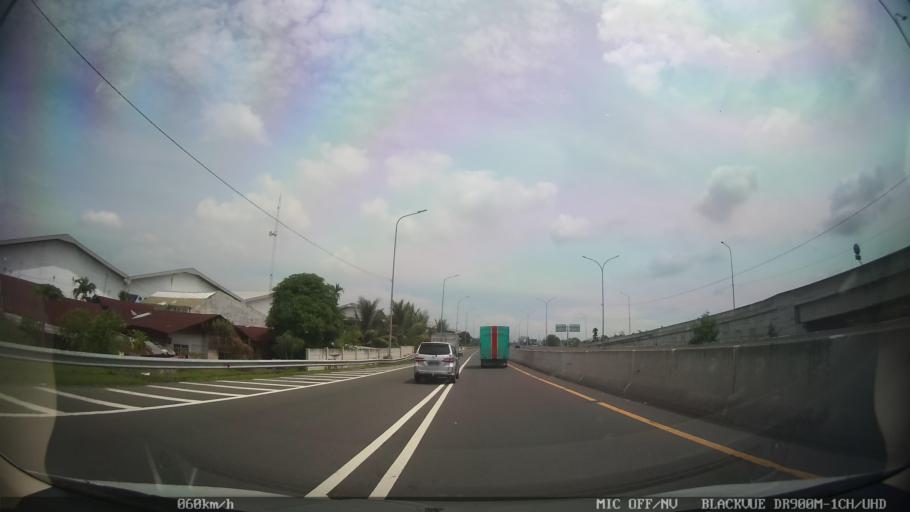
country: ID
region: North Sumatra
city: Medan
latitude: 3.6519
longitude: 98.6828
